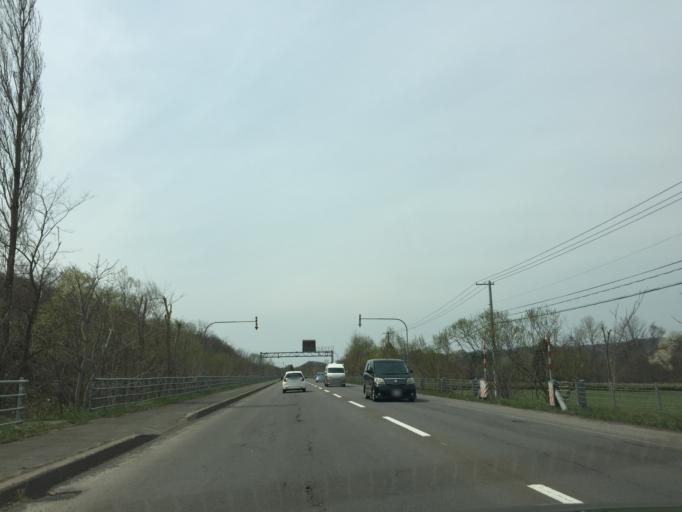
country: JP
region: Hokkaido
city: Ashibetsu
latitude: 43.5328
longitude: 142.1650
